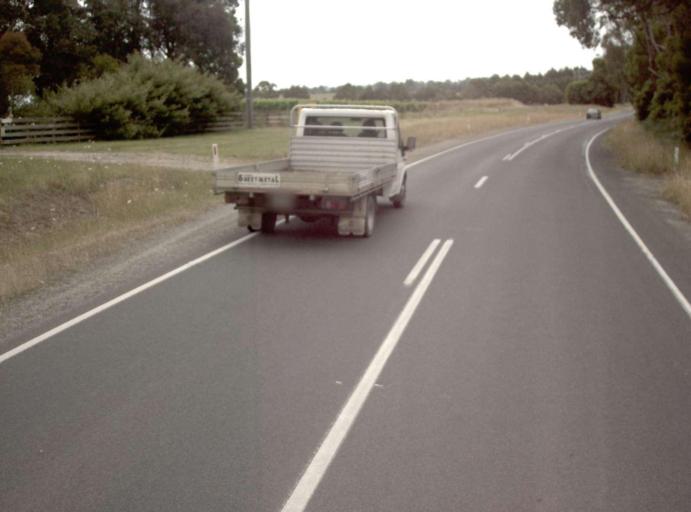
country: AU
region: Victoria
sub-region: Cardinia
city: Bunyip
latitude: -38.1751
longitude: 145.7930
